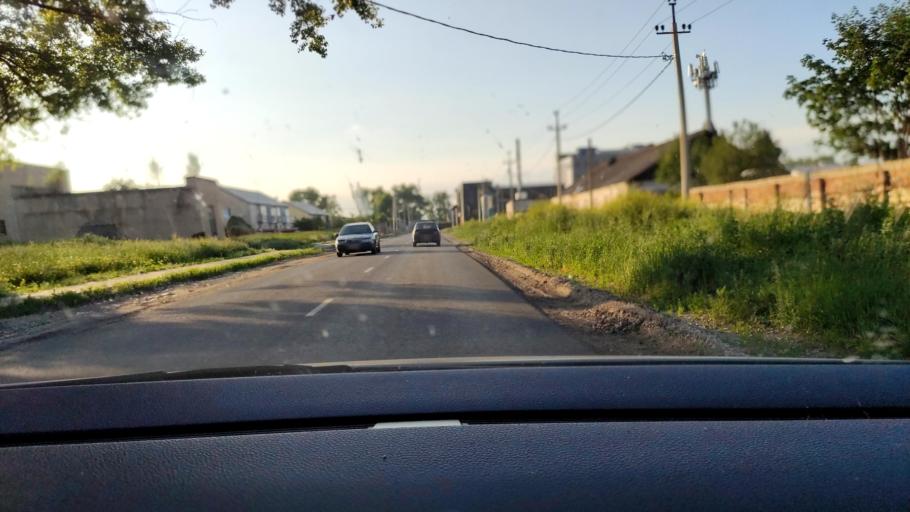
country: RU
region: Voronezj
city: Maslovka
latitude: 51.5394
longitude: 39.3412
